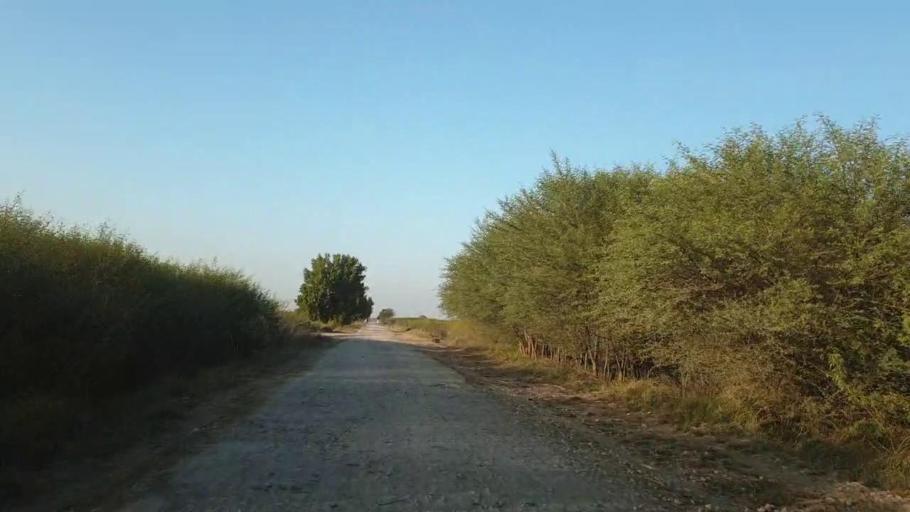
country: PK
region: Sindh
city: Mirpur Khas
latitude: 25.6683
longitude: 69.0481
